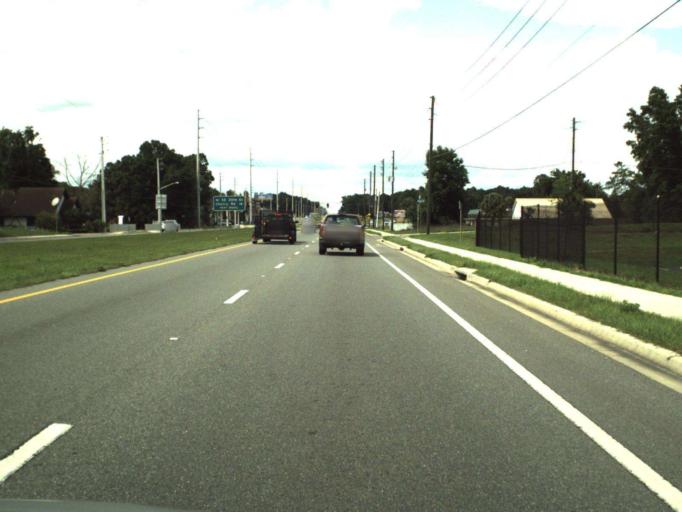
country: US
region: Florida
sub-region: Marion County
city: Silver Springs Shores
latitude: 29.1656
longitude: -82.0535
